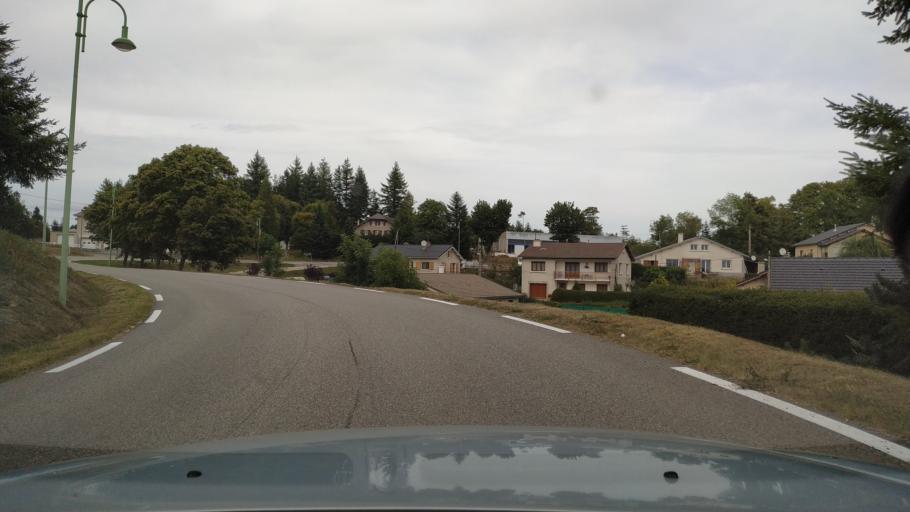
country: FR
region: Rhone-Alpes
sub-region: Departement de l'Ardeche
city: Saint-Agreve
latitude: 45.0110
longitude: 4.4014
